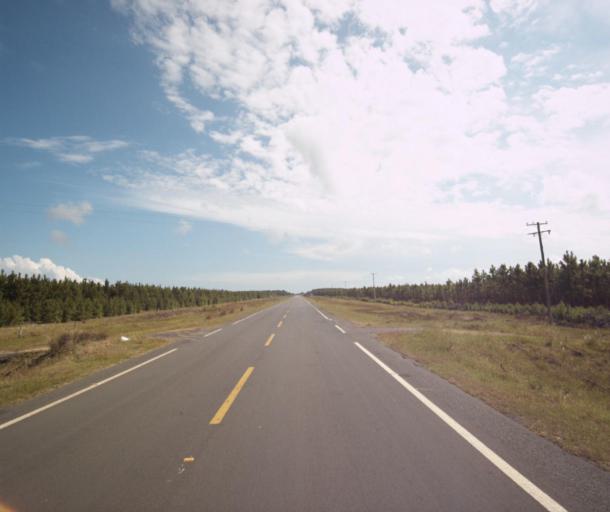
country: BR
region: Rio Grande do Sul
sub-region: Sao Lourenco Do Sul
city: Sao Lourenco do Sul
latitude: -31.5937
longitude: -51.3720
